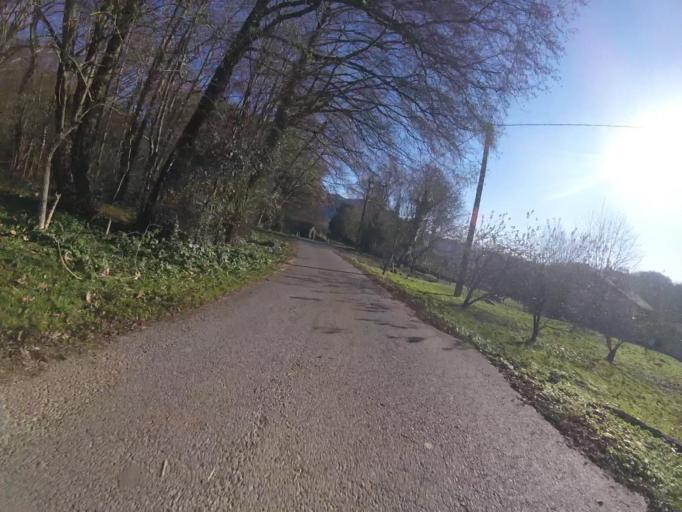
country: ES
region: Navarre
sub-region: Provincia de Navarra
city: Bera
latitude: 43.2948
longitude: -1.6488
